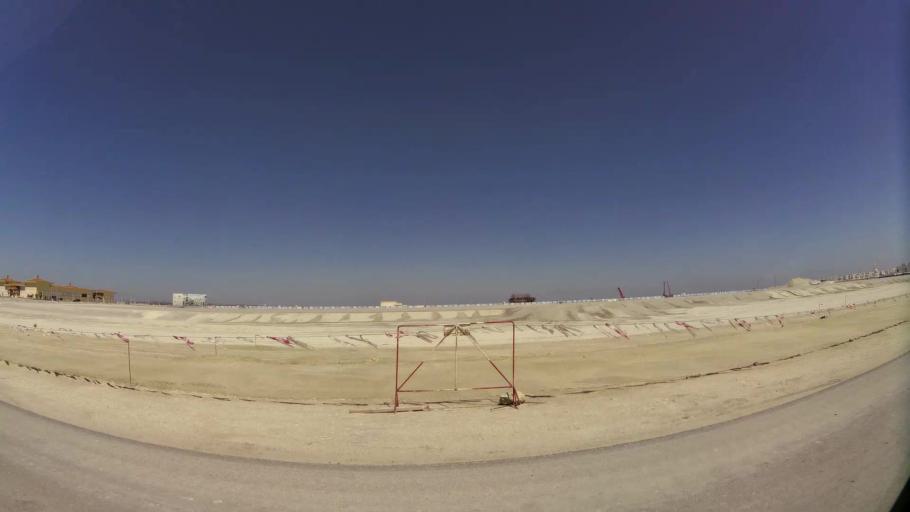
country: BH
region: Muharraq
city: Al Muharraq
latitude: 26.3025
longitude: 50.6283
